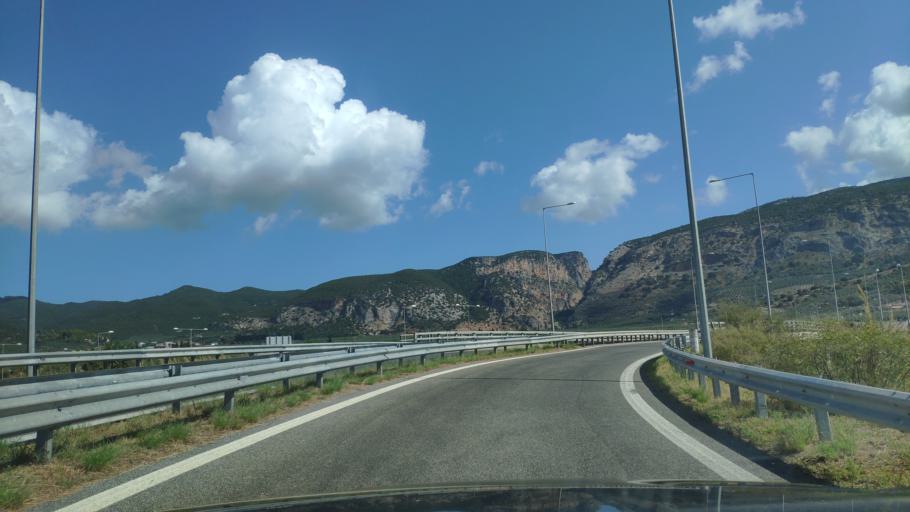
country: GR
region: West Greece
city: Aitoliko
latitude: 38.4839
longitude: 21.3450
